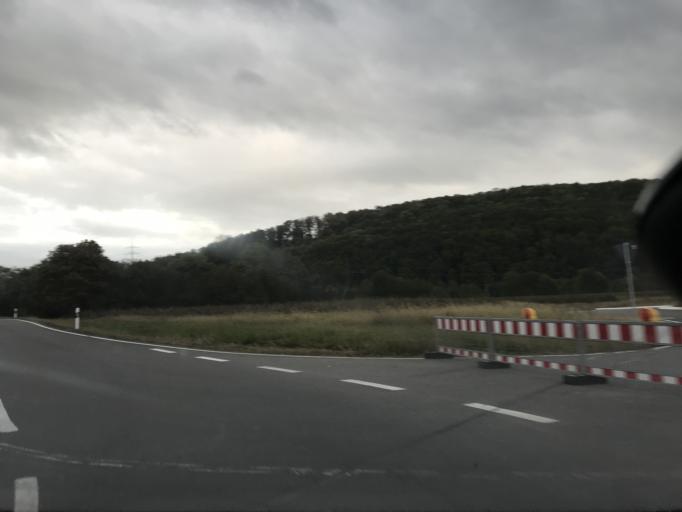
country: DE
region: Baden-Wuerttemberg
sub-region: Freiburg Region
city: Steinen
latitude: 47.6410
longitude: 7.7121
